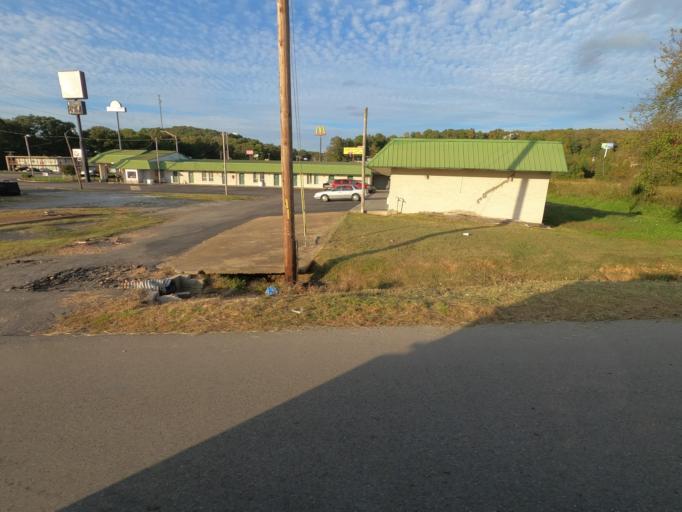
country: US
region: Tennessee
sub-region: Humphreys County
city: Waverly
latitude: 35.8824
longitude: -87.7991
